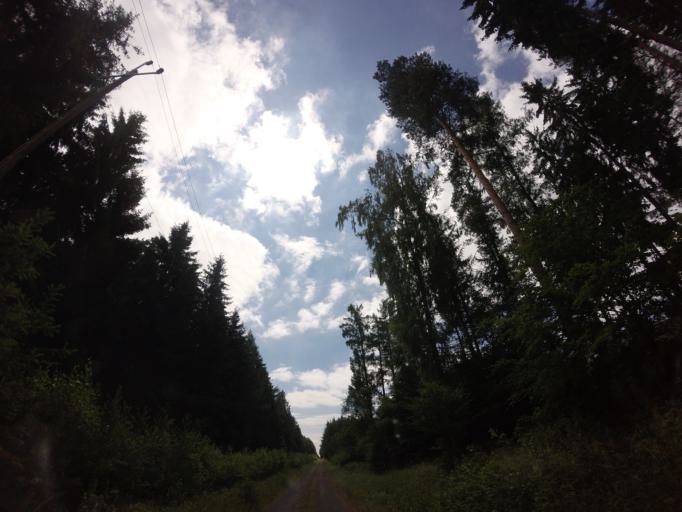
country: PL
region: West Pomeranian Voivodeship
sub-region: Powiat choszczenski
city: Krzecin
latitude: 52.9932
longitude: 15.4797
